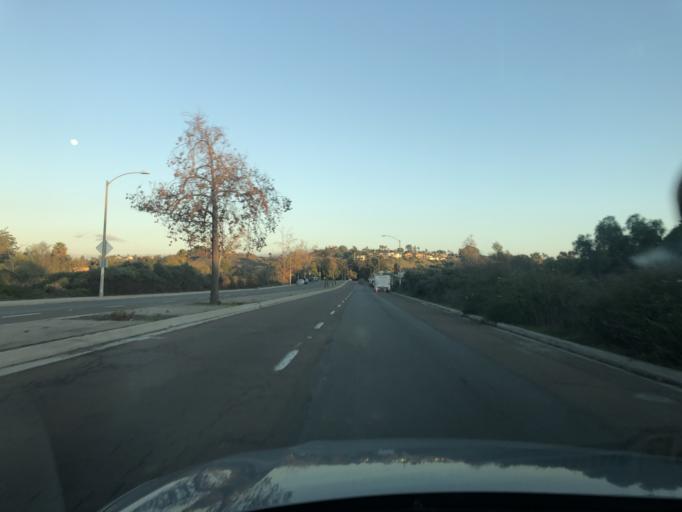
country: US
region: California
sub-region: San Diego County
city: Chula Vista
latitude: 32.6497
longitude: -117.0624
